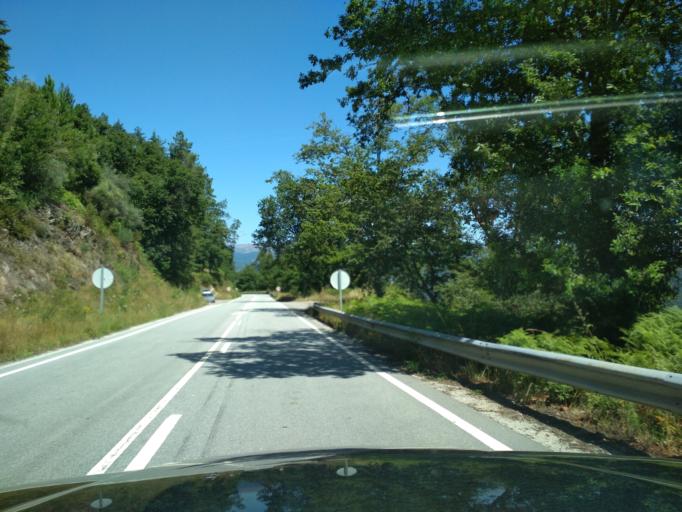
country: PT
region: Vila Real
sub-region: Ribeira de Pena
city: Ribeira de Pena
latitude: 41.5083
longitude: -7.7930
